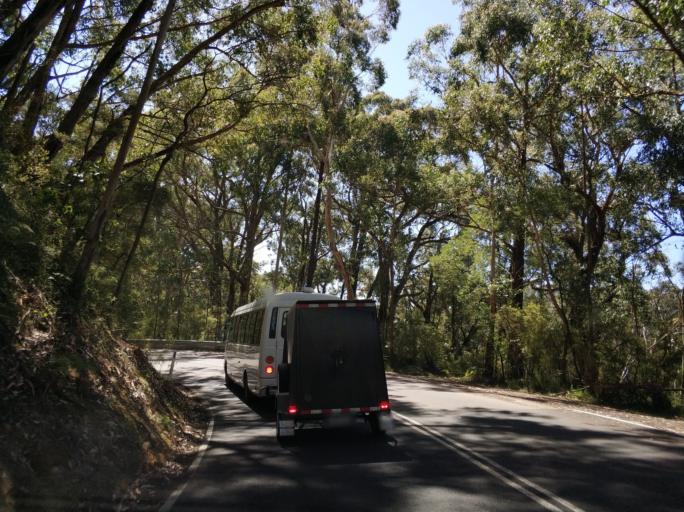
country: AU
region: Victoria
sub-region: Colac-Otway
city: Apollo Bay
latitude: -38.7459
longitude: 143.2587
